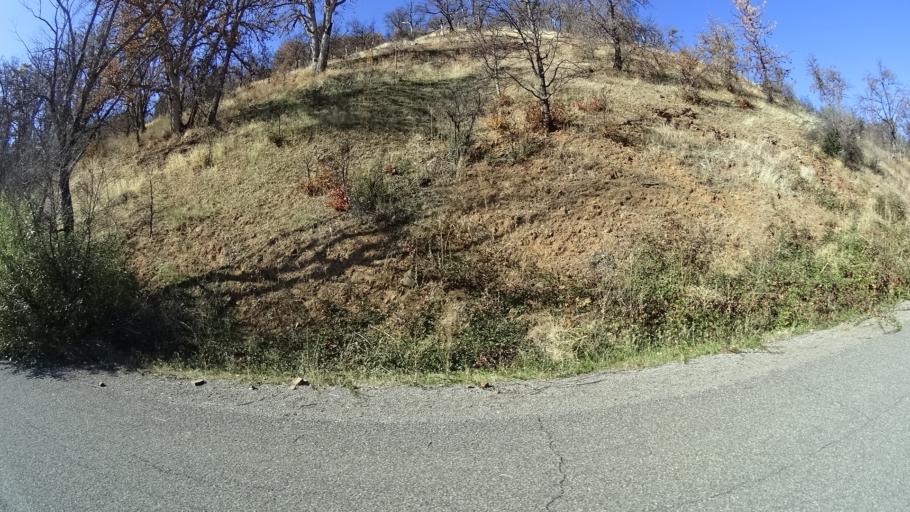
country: US
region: California
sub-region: Siskiyou County
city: Yreka
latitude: 41.9381
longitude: -122.5919
